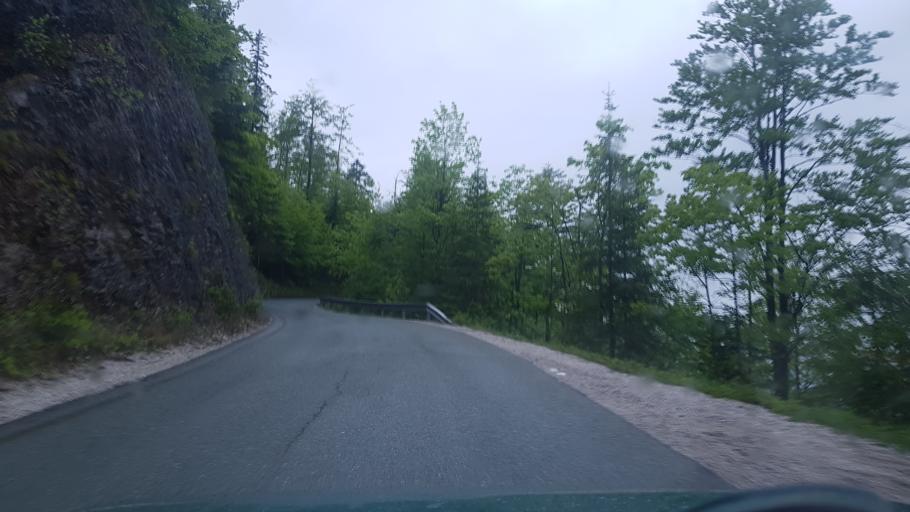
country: SI
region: Bohinj
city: Bohinjska Bistrica
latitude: 46.2659
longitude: 14.0114
